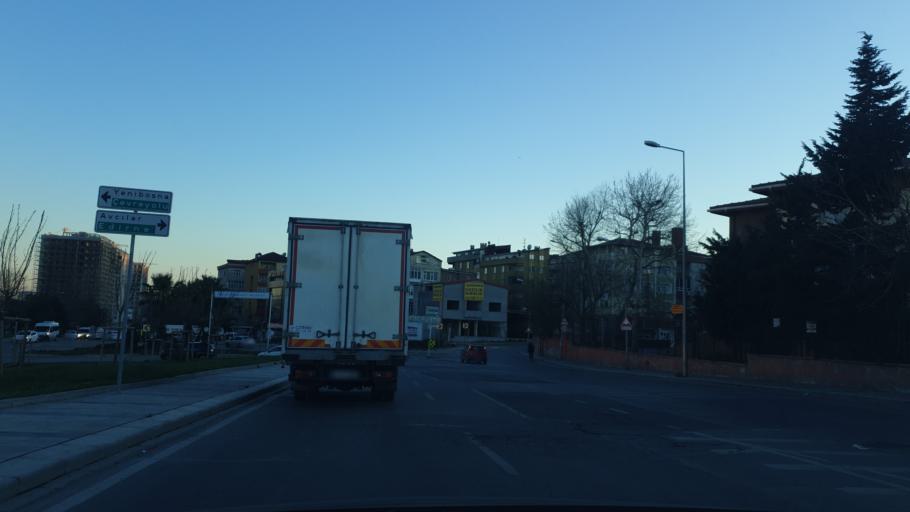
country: TR
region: Istanbul
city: Mahmutbey
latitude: 41.0076
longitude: 28.8078
